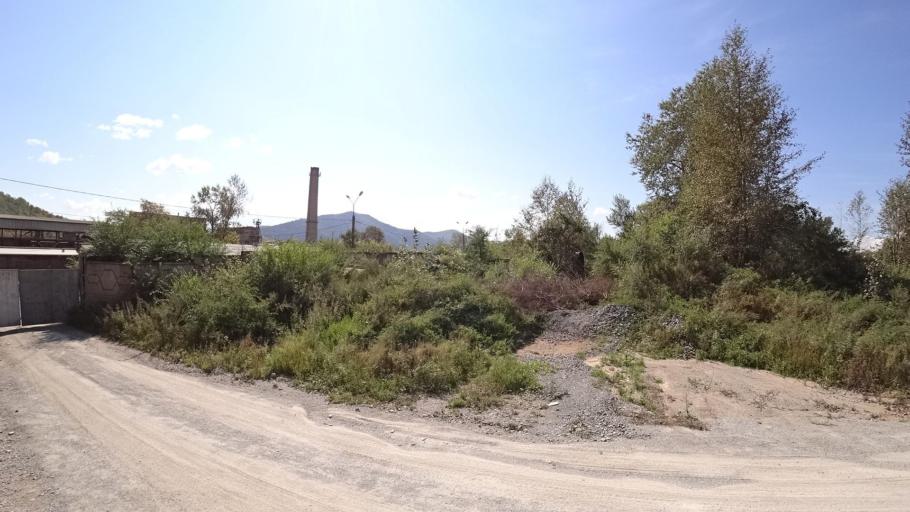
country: RU
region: Jewish Autonomous Oblast
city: Londoko
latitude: 49.0055
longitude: 131.8914
